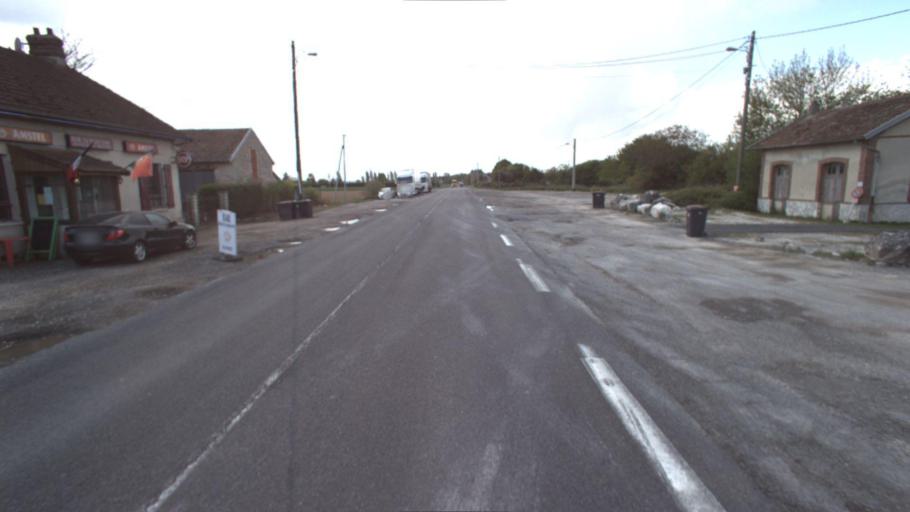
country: FR
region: Ile-de-France
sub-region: Departement de Seine-et-Marne
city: Jouy-le-Chatel
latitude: 48.6926
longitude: 3.1851
